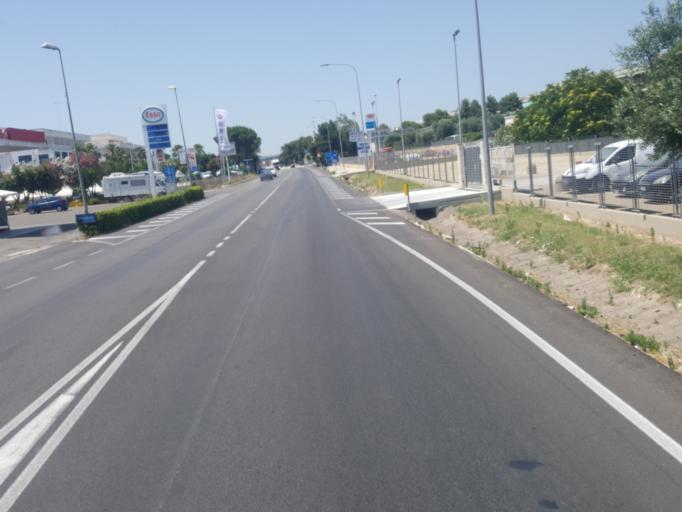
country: IT
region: Apulia
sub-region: Provincia di Taranto
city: Massafra
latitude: 40.5803
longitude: 17.1145
